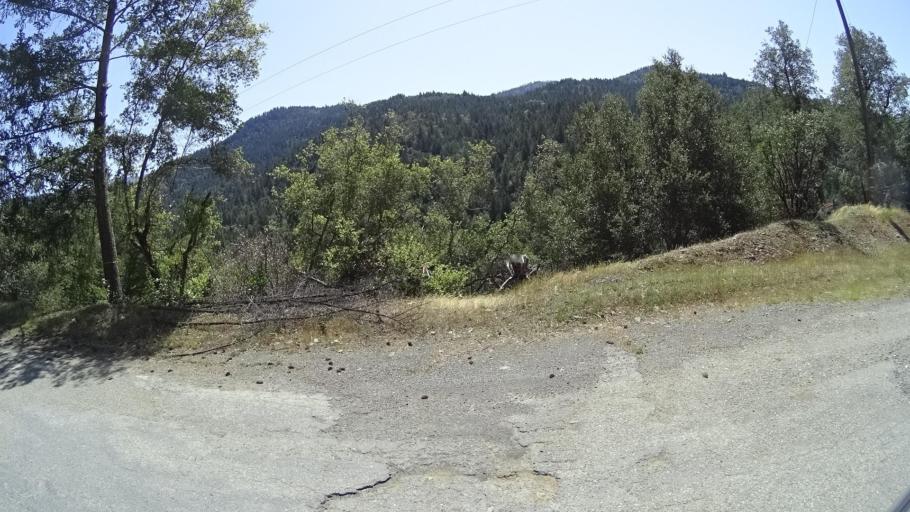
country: US
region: California
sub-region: Humboldt County
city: Redway
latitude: 40.1926
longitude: -123.5461
